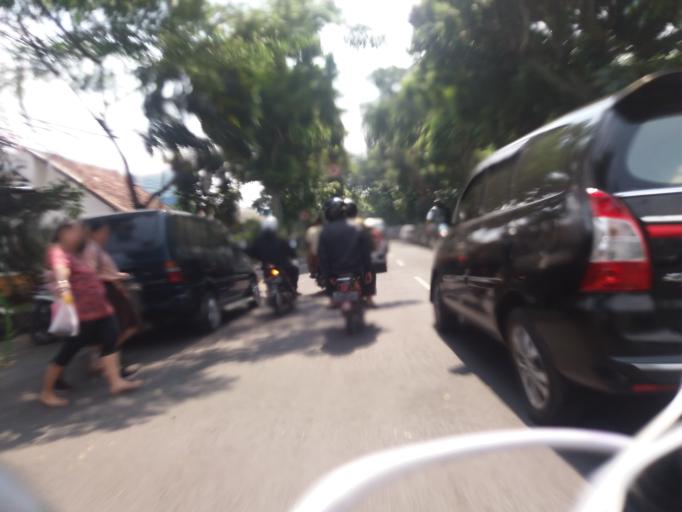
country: ID
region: West Java
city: Bandung
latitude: -6.9126
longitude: 107.6131
